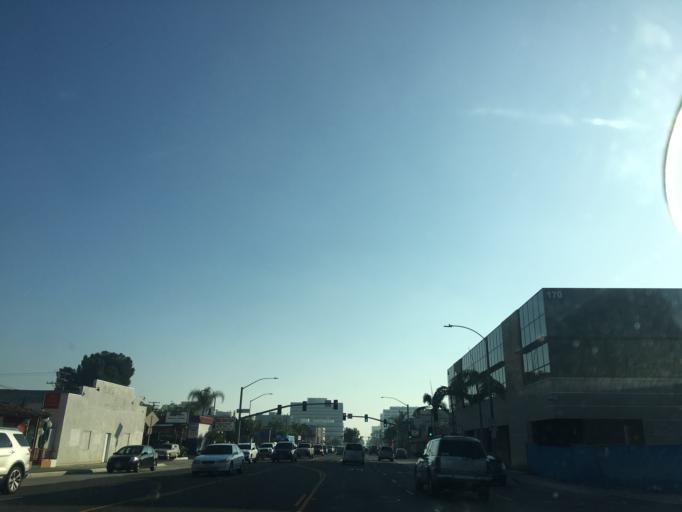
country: US
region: California
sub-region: Orange County
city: Orange
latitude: 33.7873
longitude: -117.8676
